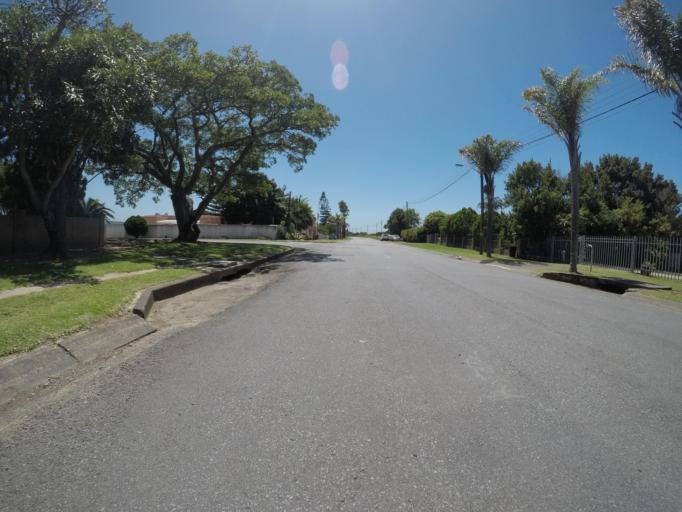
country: ZA
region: Eastern Cape
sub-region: Buffalo City Metropolitan Municipality
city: East London
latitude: -32.9659
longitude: 27.9491
